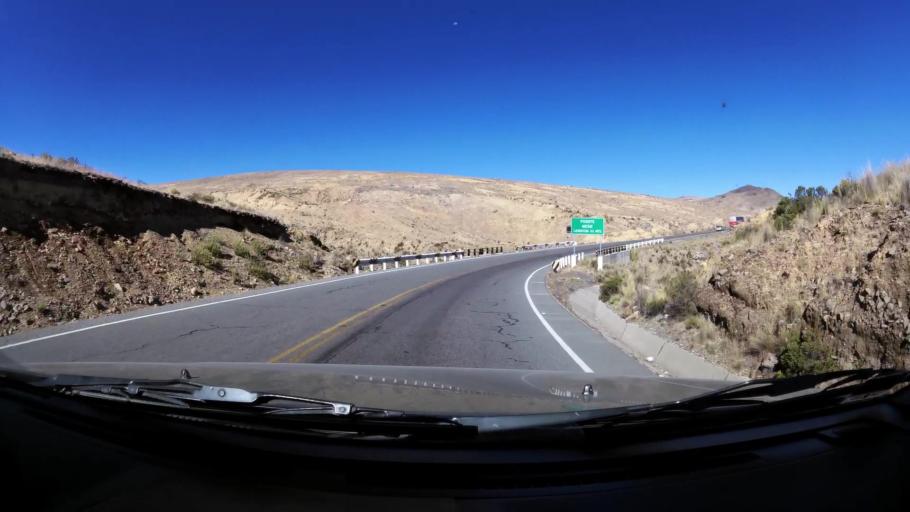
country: PE
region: Huancavelica
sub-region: Huaytara
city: Huayacundo Arma
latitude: -13.5504
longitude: -75.2228
